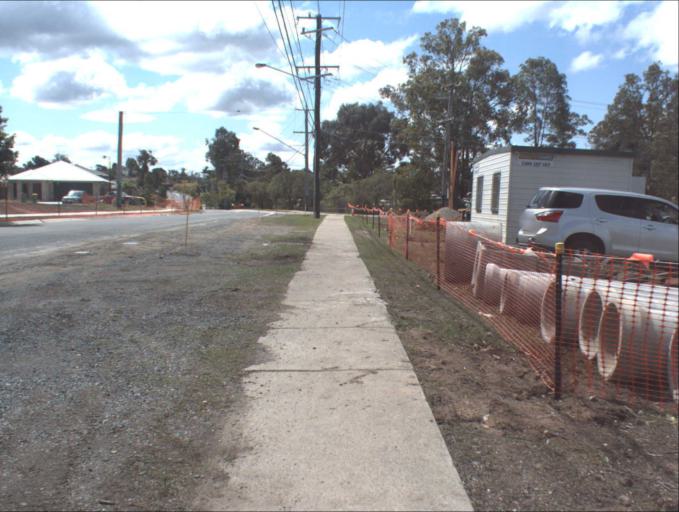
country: AU
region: Queensland
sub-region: Logan
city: Park Ridge South
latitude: -27.6708
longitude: 153.0227
